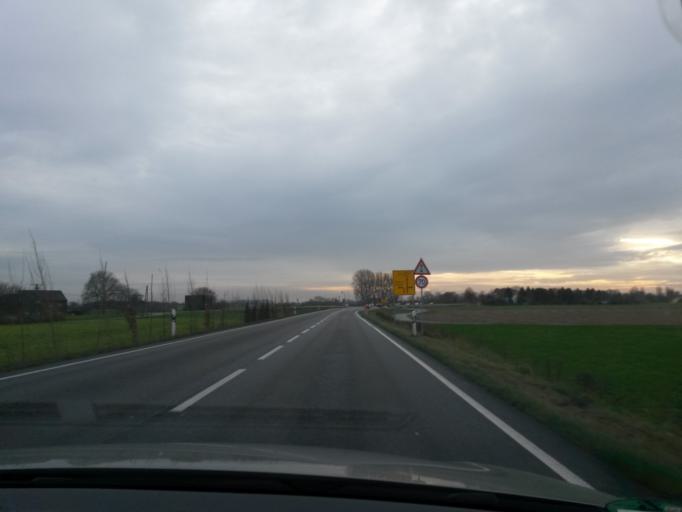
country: DE
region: North Rhine-Westphalia
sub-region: Regierungsbezirk Dusseldorf
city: Alpen
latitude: 51.6166
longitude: 6.5623
